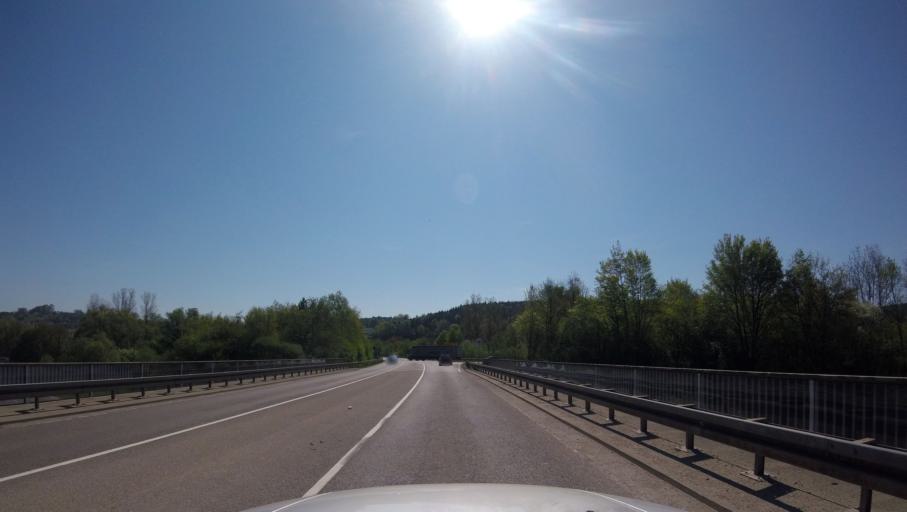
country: DE
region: Baden-Wuerttemberg
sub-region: Regierungsbezirk Stuttgart
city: Schwabisch Gmund
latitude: 48.7881
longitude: 9.7622
